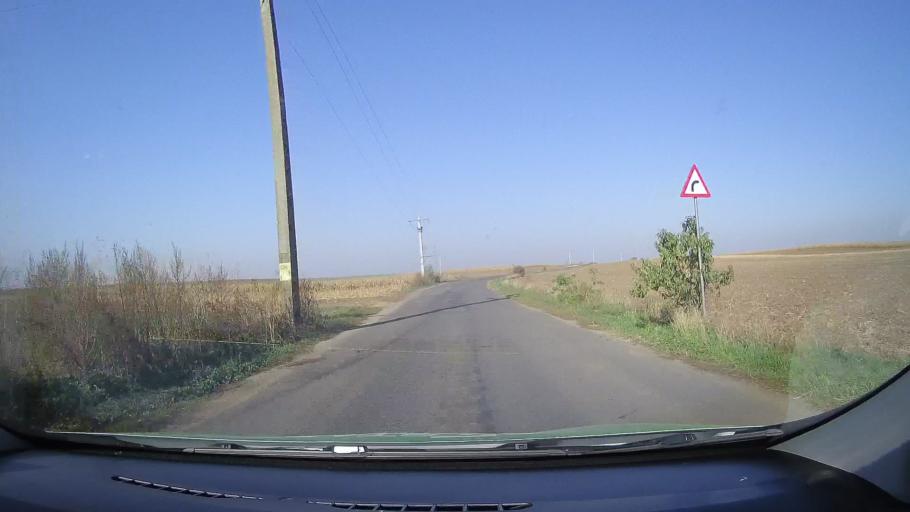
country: RO
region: Satu Mare
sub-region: Comuna Petresti
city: Petresti
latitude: 47.6101
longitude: 22.3547
